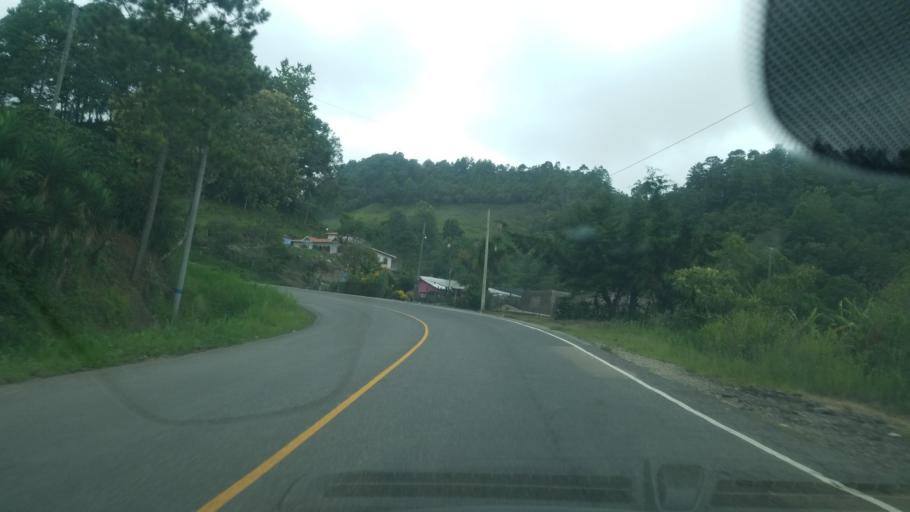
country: HN
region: Ocotepeque
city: La Labor
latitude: 14.4816
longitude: -89.0580
